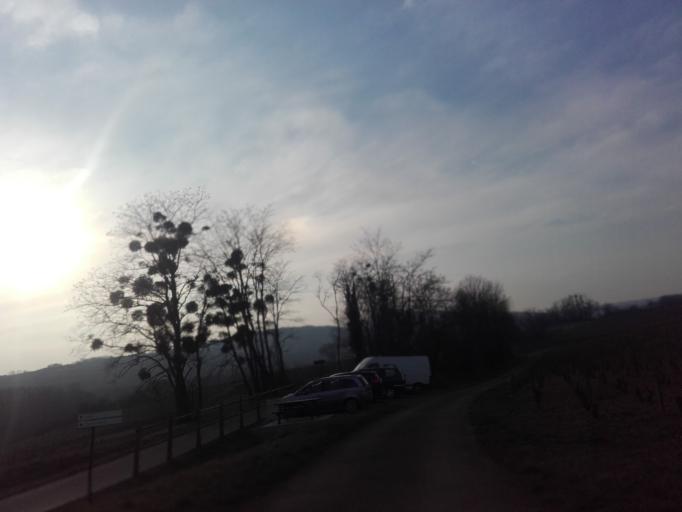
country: FR
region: Bourgogne
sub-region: Departement de la Cote-d'Or
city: Nolay
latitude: 46.9011
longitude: 4.6719
